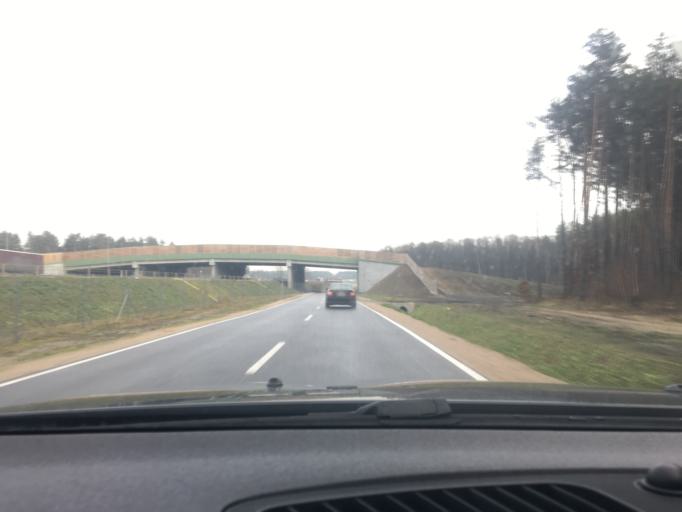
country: PL
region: Swietokrzyskie
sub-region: Powiat jedrzejowski
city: Jedrzejow
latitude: 50.6766
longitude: 20.3502
